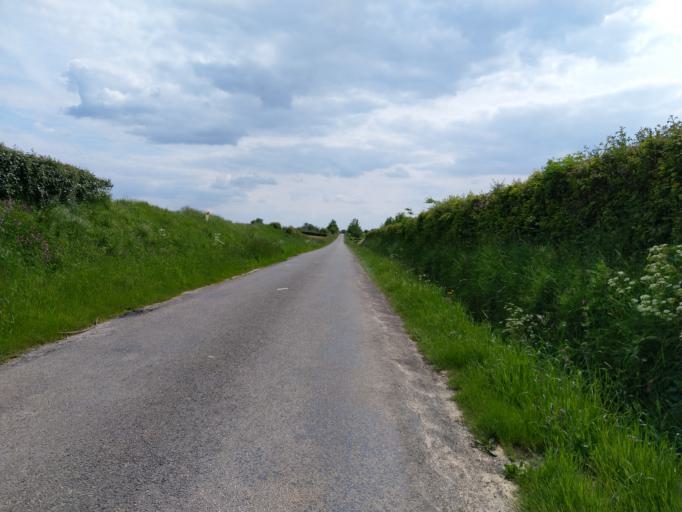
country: FR
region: Picardie
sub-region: Departement de l'Aisne
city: Boue
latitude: 50.0332
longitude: 3.6803
